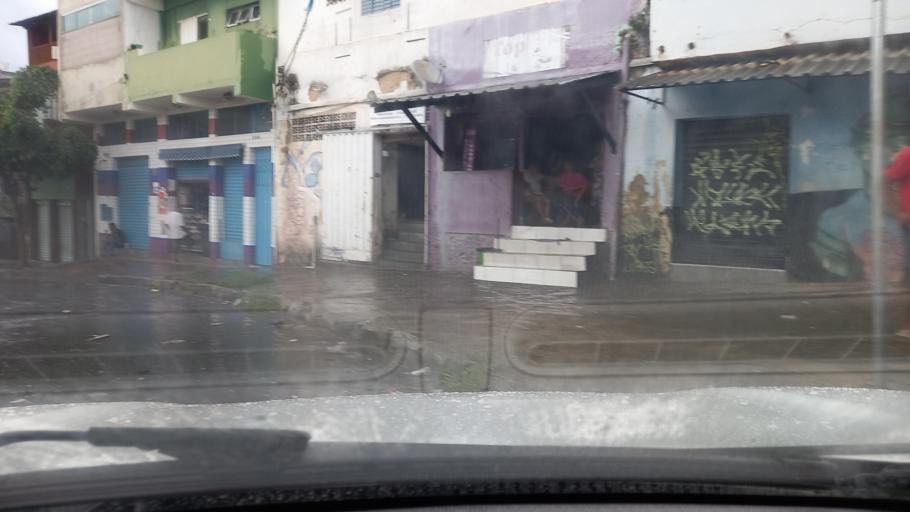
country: BR
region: Minas Gerais
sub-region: Belo Horizonte
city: Belo Horizonte
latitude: -19.9014
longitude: -43.9483
